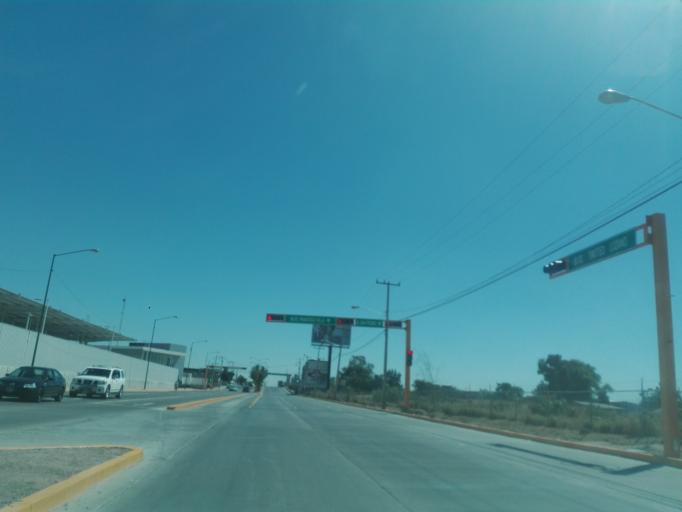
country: MX
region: Guanajuato
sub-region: Leon
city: San Jose de Duran (Los Troncoso)
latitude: 21.0908
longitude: -101.6774
